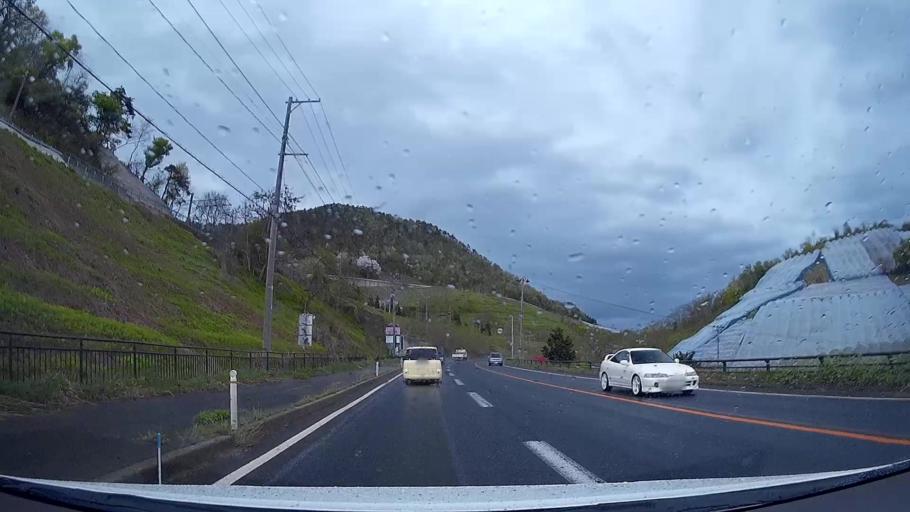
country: JP
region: Yamagata
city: Takahata
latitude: 38.0638
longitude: 140.1769
